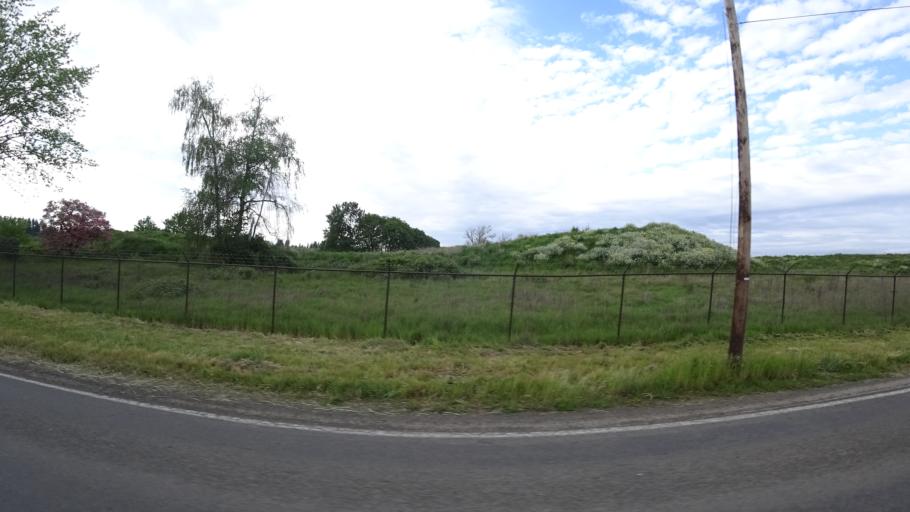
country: US
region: Oregon
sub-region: Washington County
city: Hillsboro
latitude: 45.4869
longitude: -122.9770
